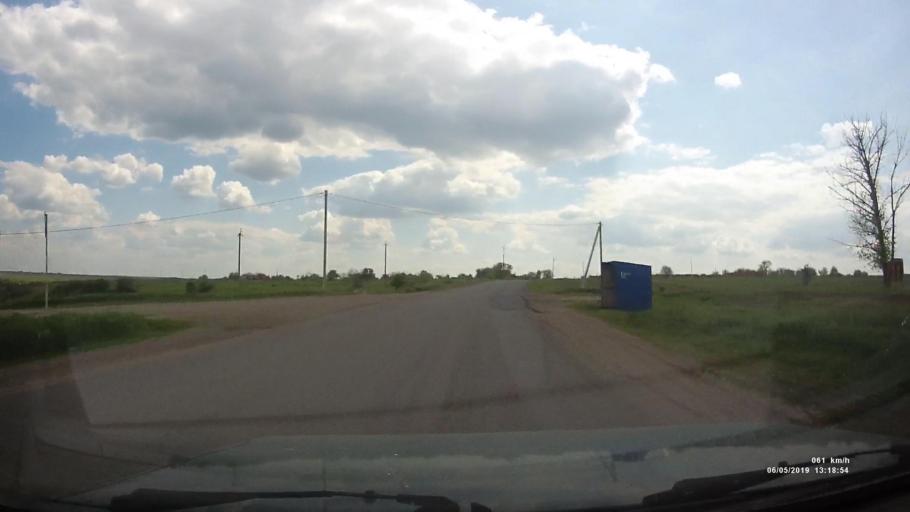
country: RU
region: Rostov
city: Ust'-Donetskiy
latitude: 47.7305
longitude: 40.9146
